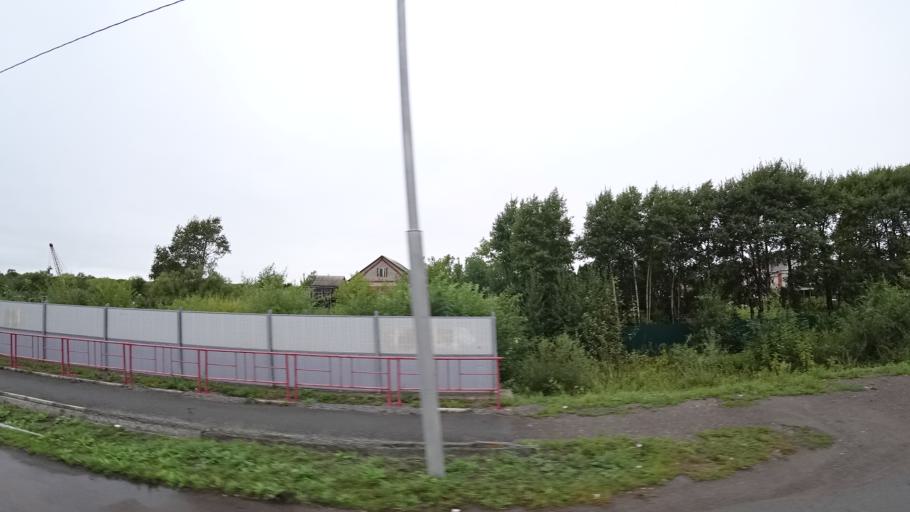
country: RU
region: Primorskiy
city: Monastyrishche
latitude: 44.2000
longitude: 132.4485
